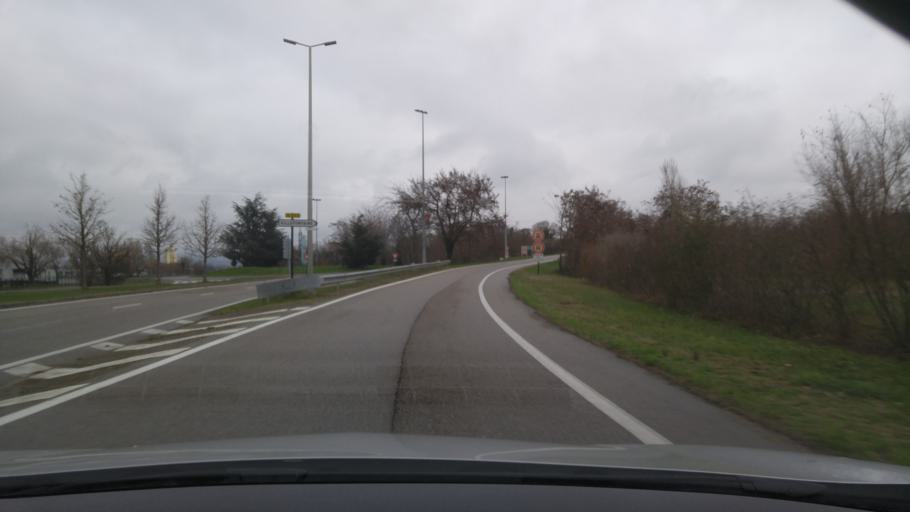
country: FR
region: Rhone-Alpes
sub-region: Departement de l'Isere
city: Saint-Quentin-Fallavier
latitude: 45.6399
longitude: 5.1205
